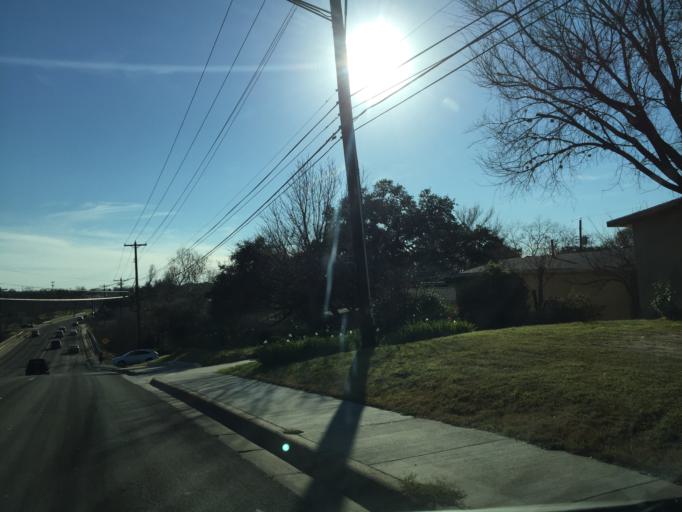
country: US
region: Texas
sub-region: Travis County
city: Austin
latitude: 30.2166
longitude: -97.7758
